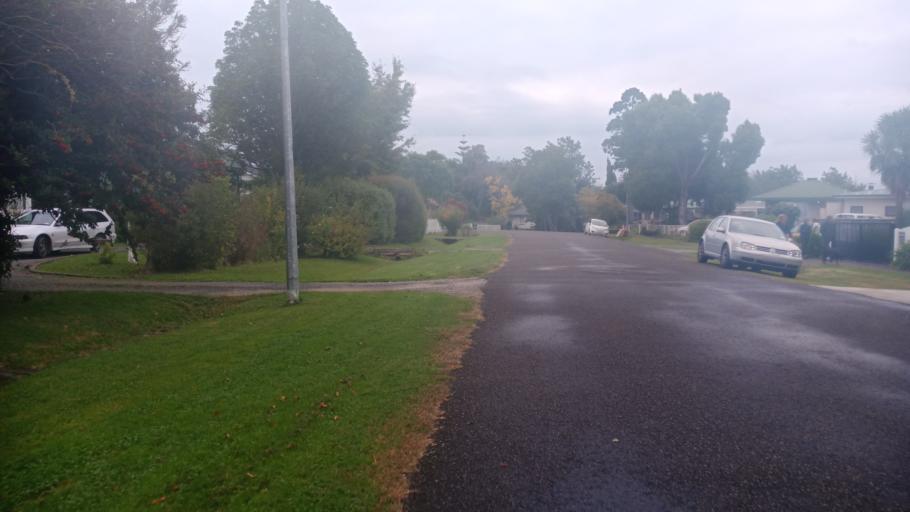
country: NZ
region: Gisborne
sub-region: Gisborne District
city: Gisborne
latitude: -38.6650
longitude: 178.0344
